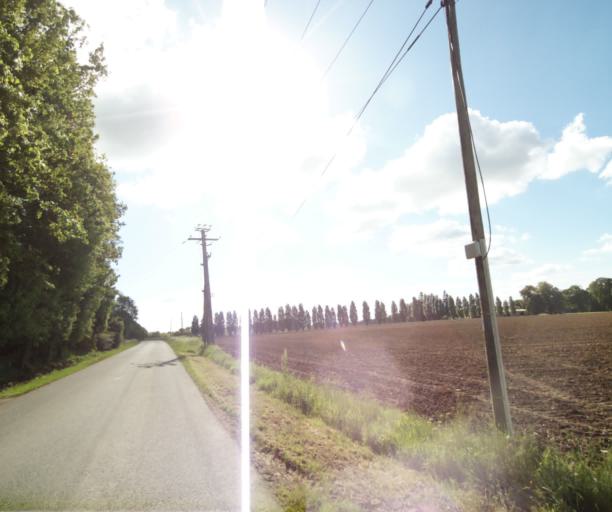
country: FR
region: Poitou-Charentes
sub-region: Departement de la Charente-Maritime
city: Chermignac
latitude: 45.7143
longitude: -0.7064
